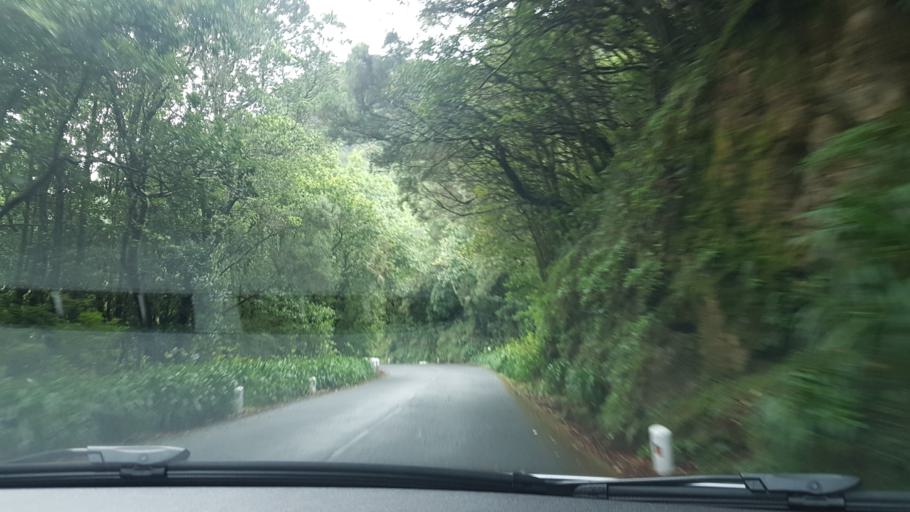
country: PT
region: Madeira
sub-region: Sao Vicente
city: Sao Vicente
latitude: 32.7551
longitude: -17.0167
